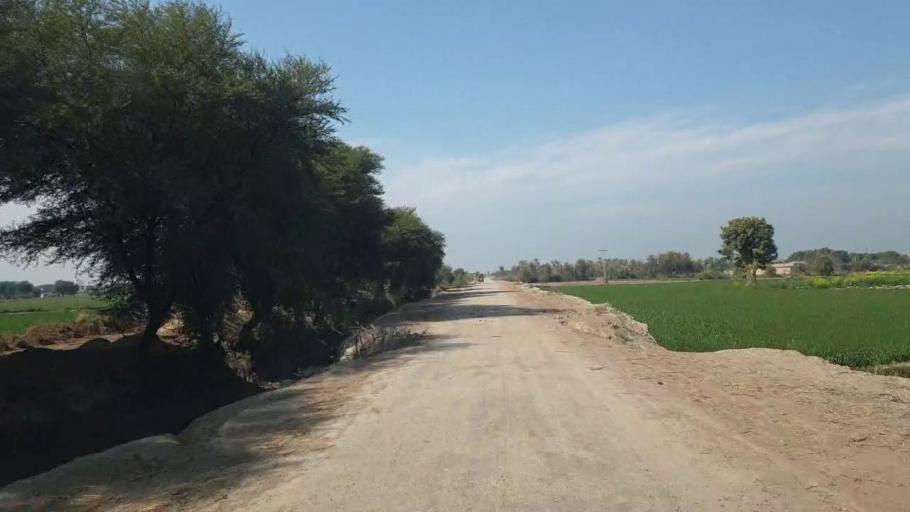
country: PK
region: Sindh
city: Shahdadpur
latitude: 25.9946
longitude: 68.5273
